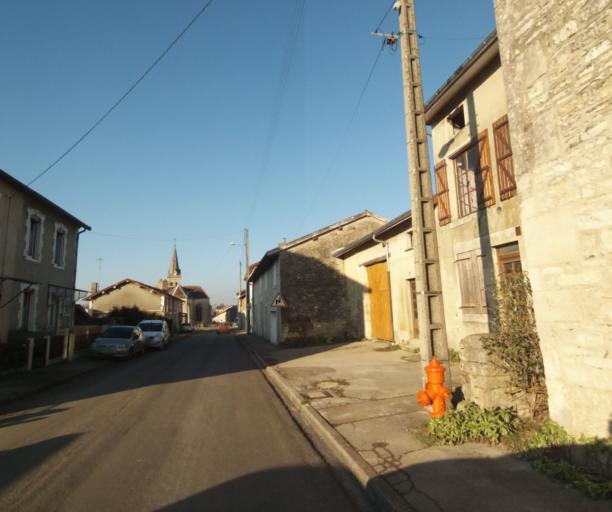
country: FR
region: Champagne-Ardenne
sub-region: Departement de la Haute-Marne
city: Bienville
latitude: 48.5711
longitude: 5.0463
